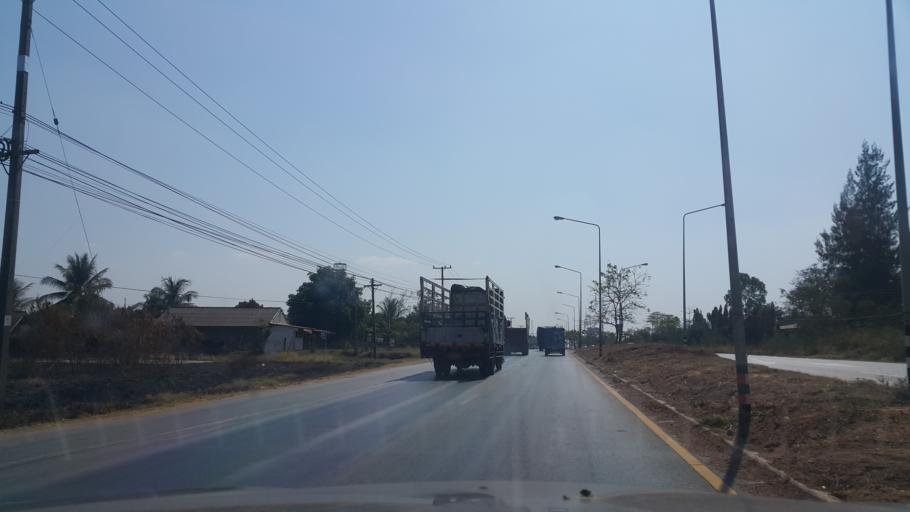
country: TH
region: Changwat Udon Thani
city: Non Sa-at
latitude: 16.9910
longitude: 102.8931
